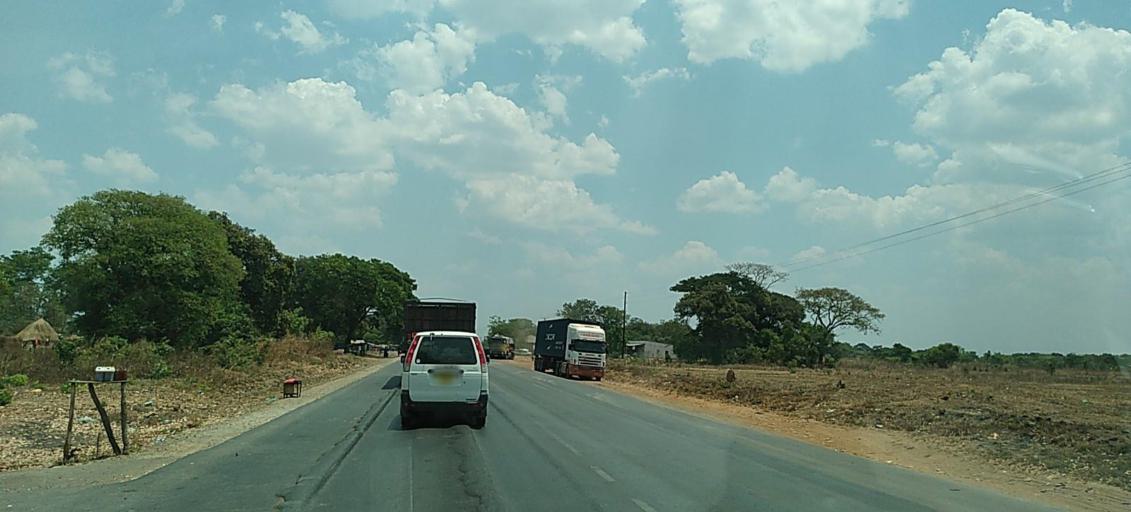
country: ZM
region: Central
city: Kabwe
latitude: -14.2201
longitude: 28.5771
